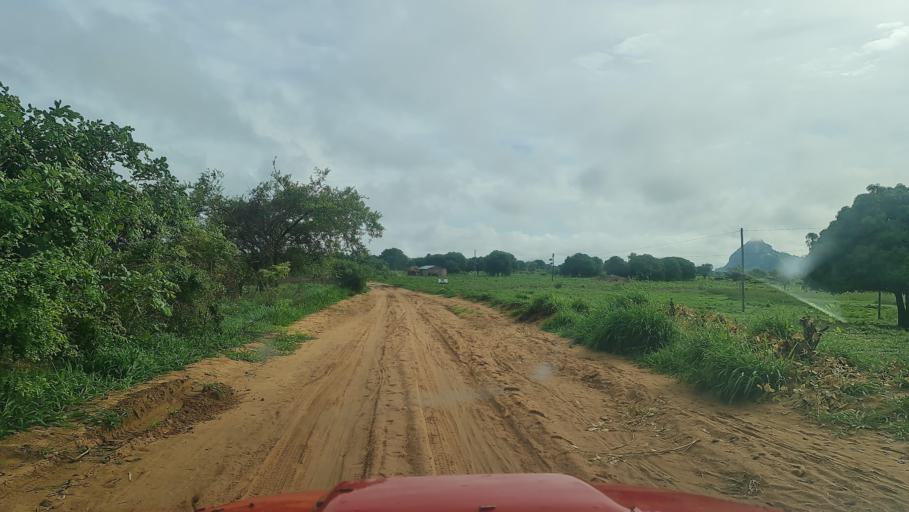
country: MW
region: Southern Region
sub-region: Nsanje District
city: Nsanje
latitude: -17.2796
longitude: 35.6168
